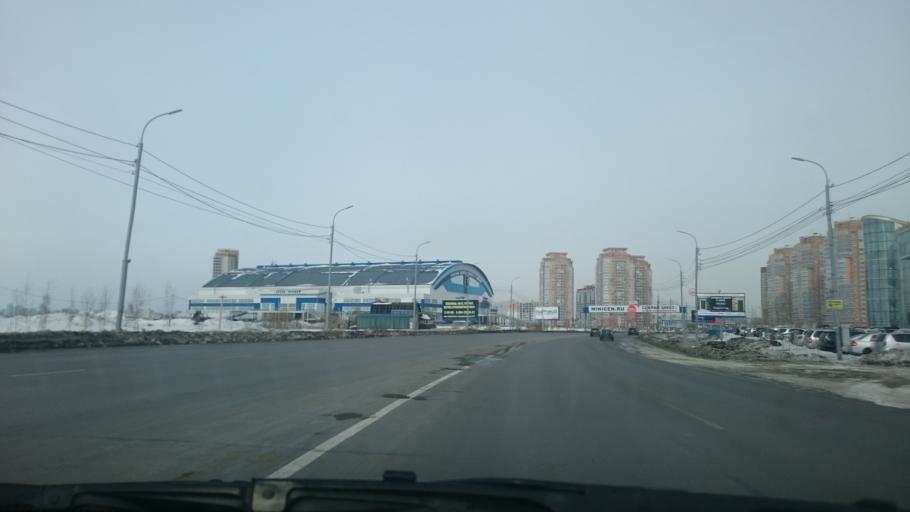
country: RU
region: Khabarovsk Krai
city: Khabarovsk Vtoroy
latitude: 48.4275
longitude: 135.1008
